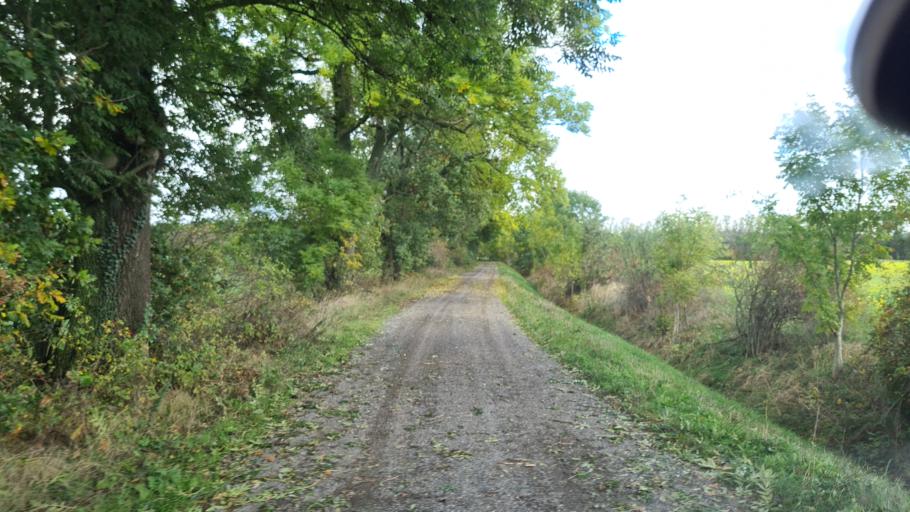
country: DE
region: Brandenburg
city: Sallgast
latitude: 51.6007
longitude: 13.8955
